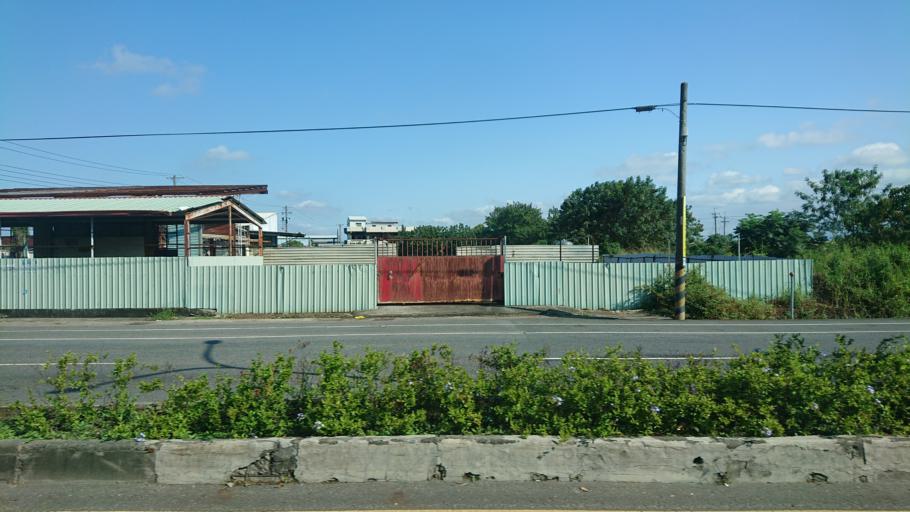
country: TW
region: Taiwan
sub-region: Chiayi
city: Taibao
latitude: 23.4372
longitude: 120.3885
